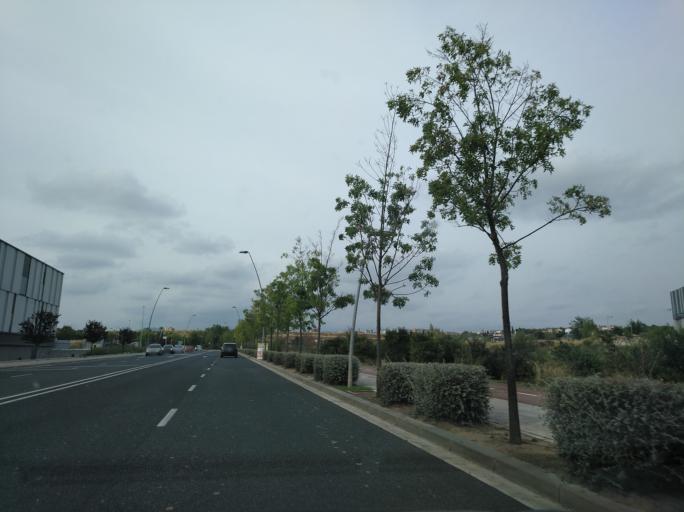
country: ES
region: Catalonia
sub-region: Provincia de Barcelona
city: Barbera del Valles
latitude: 41.5119
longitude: 2.1084
